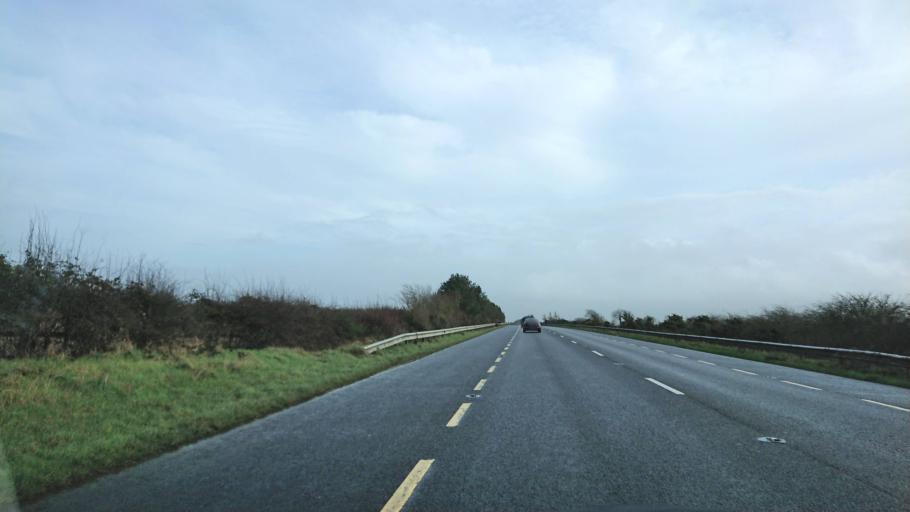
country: IE
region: Leinster
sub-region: Loch Garman
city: Enniscorthy
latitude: 52.3511
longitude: -6.6579
